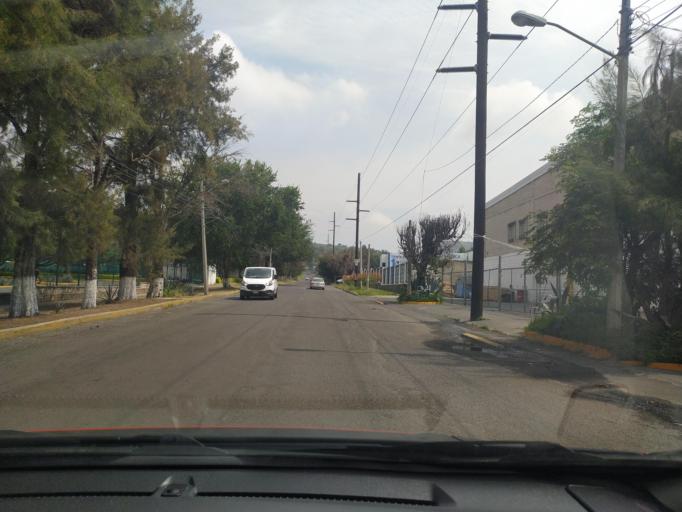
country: MX
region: Jalisco
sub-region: Tlajomulco de Zuniga
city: La Tijera
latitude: 20.6030
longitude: -103.4061
